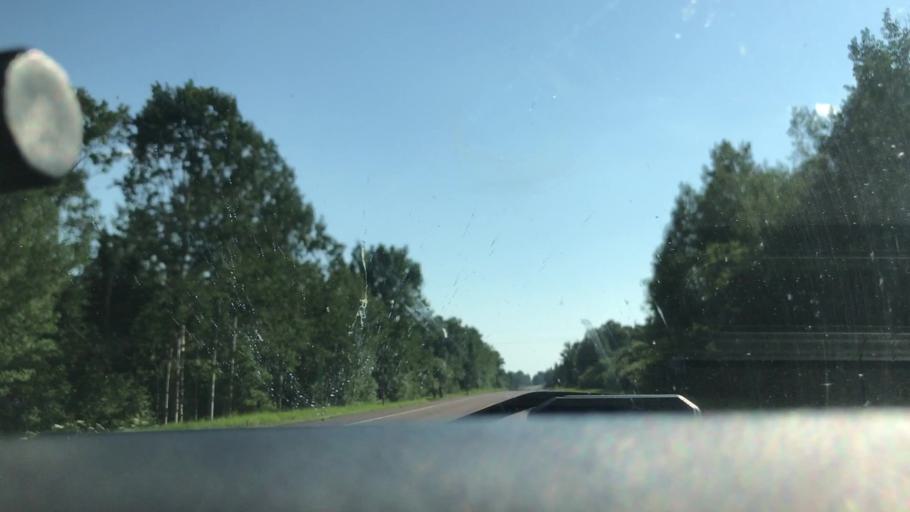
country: US
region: Minnesota
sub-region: Cook County
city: Grand Marais
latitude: 47.8059
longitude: -90.0912
